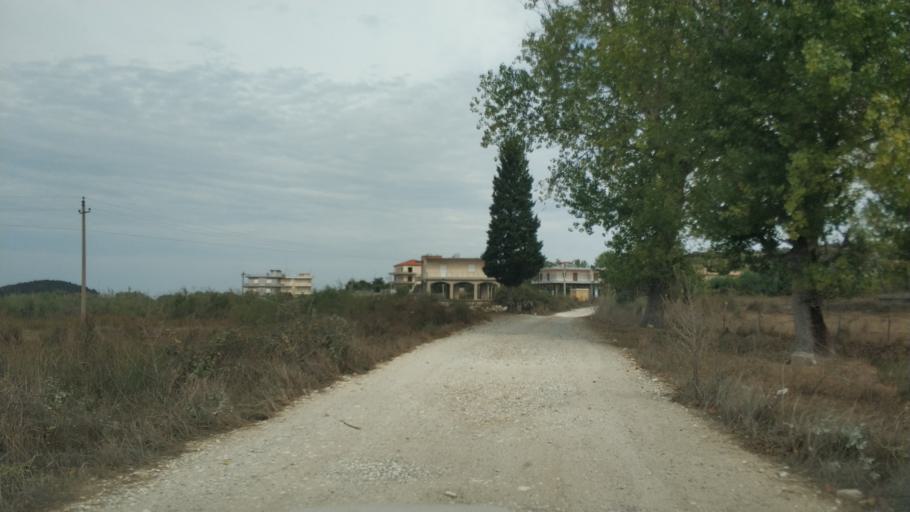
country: AL
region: Vlore
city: Vlore
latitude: 40.5062
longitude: 19.4112
